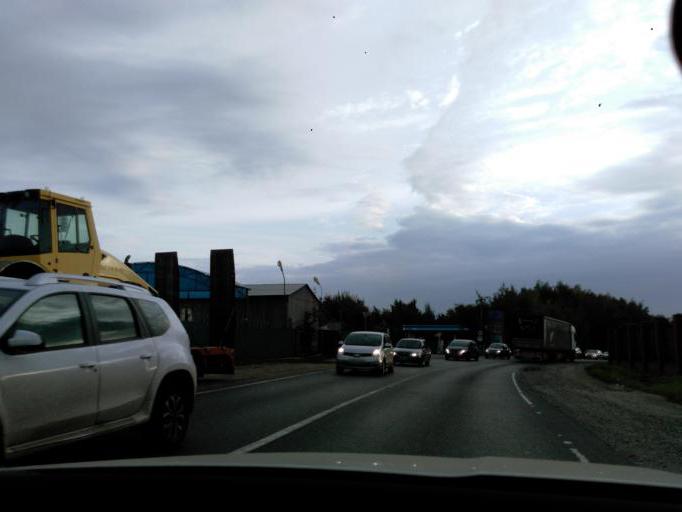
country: RU
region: Moskovskaya
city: Sheremet'yevskiy
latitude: 55.9716
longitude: 37.4505
